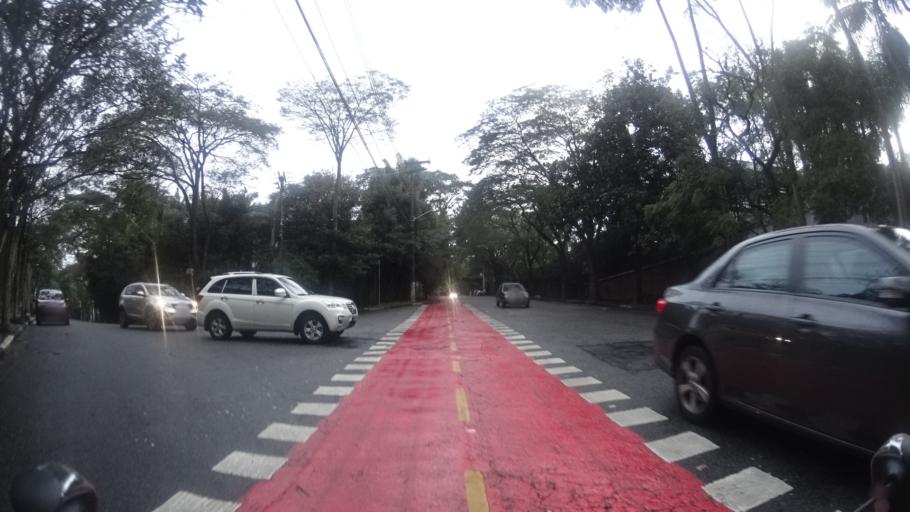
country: BR
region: Sao Paulo
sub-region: Sao Paulo
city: Sao Paulo
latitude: -23.5827
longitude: -46.7041
